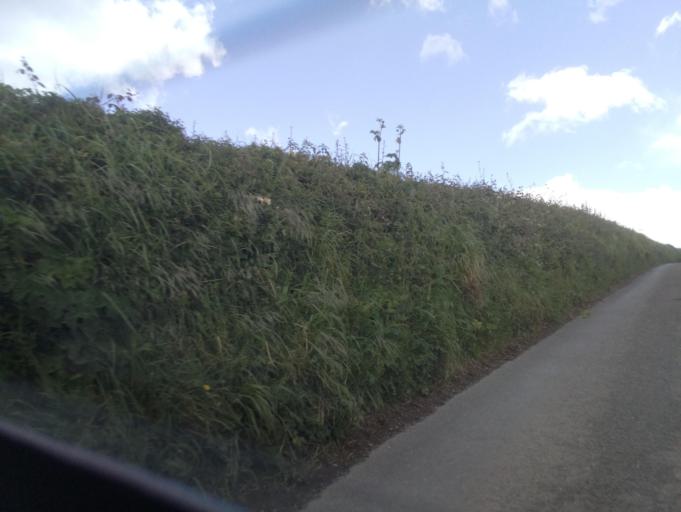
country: GB
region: England
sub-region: Devon
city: Dartmouth
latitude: 50.3529
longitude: -3.5384
